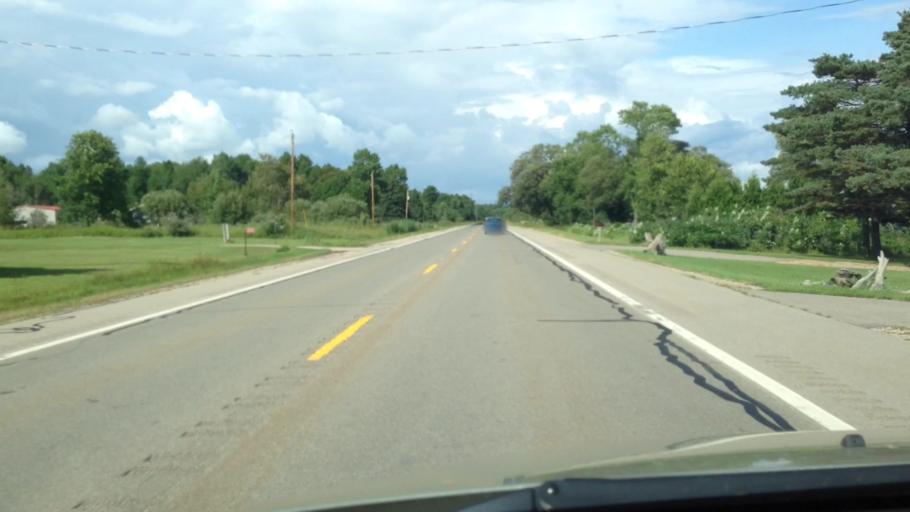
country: US
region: Michigan
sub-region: Menominee County
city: Menominee
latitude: 45.2464
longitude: -87.4913
